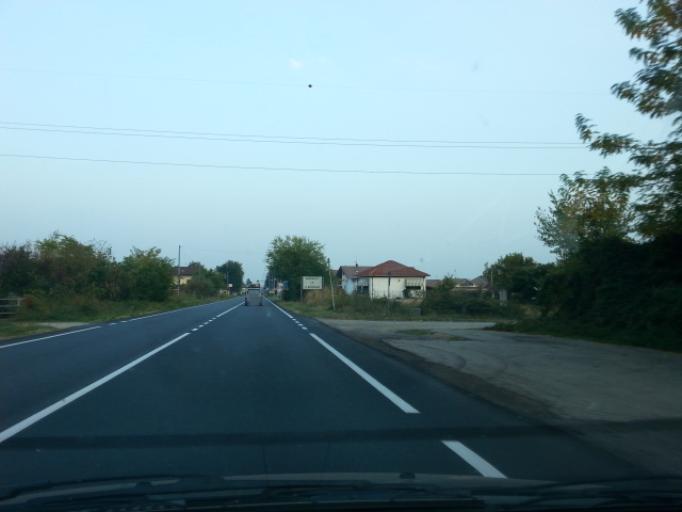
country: IT
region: Piedmont
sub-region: Provincia di Torino
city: Sangano
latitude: 45.0308
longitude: 7.4408
